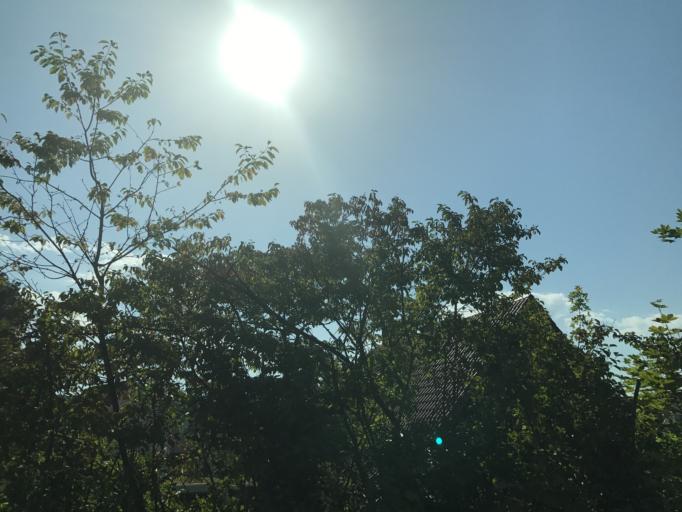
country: DE
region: Baden-Wuerttemberg
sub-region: Tuebingen Region
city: Wangen im Allgau
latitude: 47.6895
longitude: 9.8372
